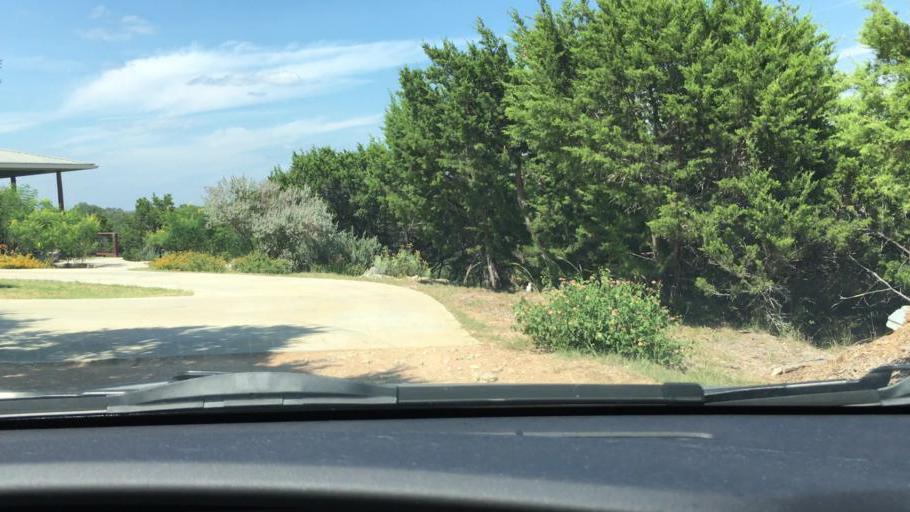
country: US
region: Texas
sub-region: Travis County
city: Shady Hollow
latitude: 30.1716
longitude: -97.9701
